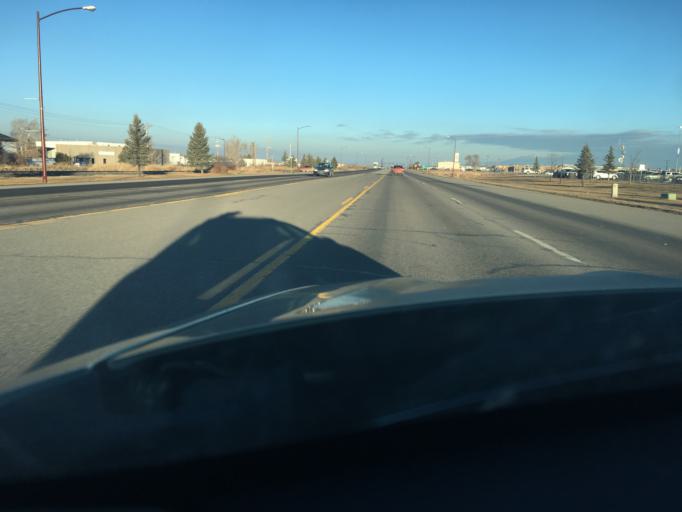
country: US
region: Colorado
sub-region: Montrose County
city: Montrose
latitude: 38.4993
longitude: -107.9004
